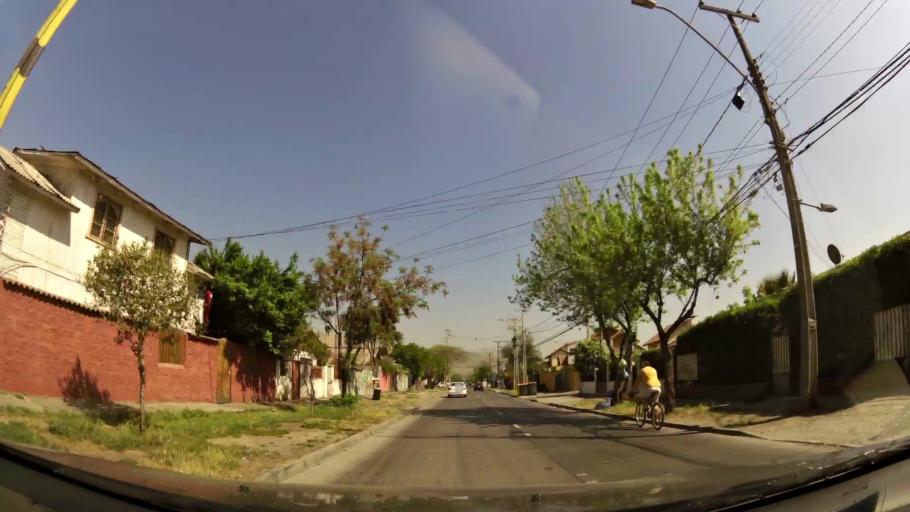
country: CL
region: Santiago Metropolitan
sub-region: Provincia de Maipo
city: San Bernardo
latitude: -33.5854
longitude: -70.7031
